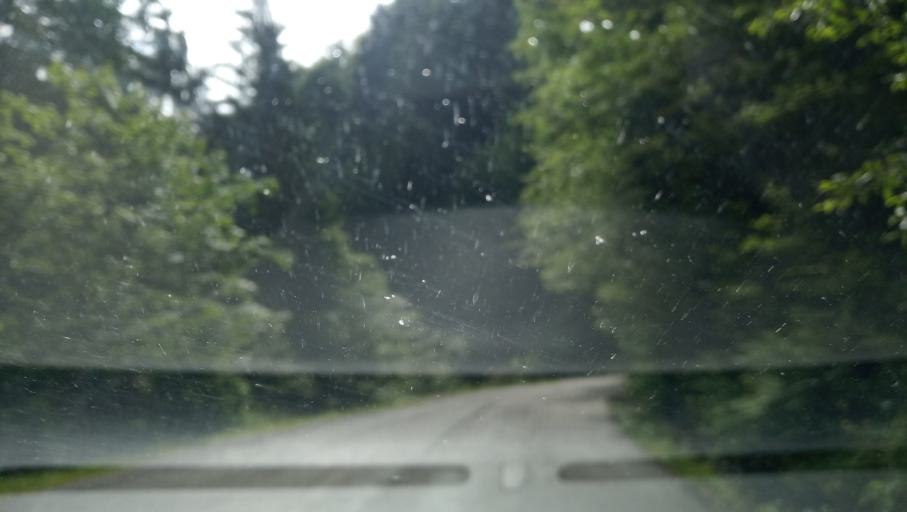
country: RO
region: Hunedoara
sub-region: Oras Petrila
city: Petrila
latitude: 45.4097
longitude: 23.4956
